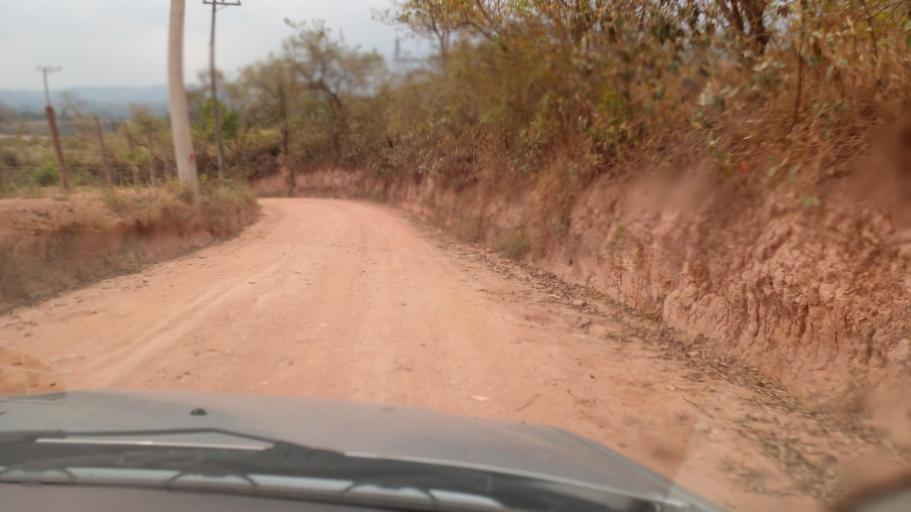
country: BR
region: Sao Paulo
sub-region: Louveira
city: Louveira
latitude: -23.1281
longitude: -46.9075
